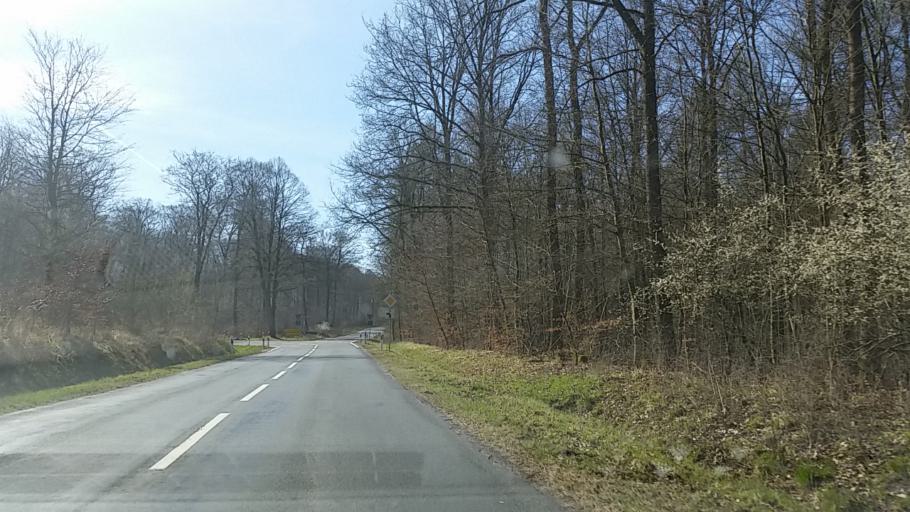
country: DE
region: Lower Saxony
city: Rabke
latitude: 52.1686
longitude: 10.8575
